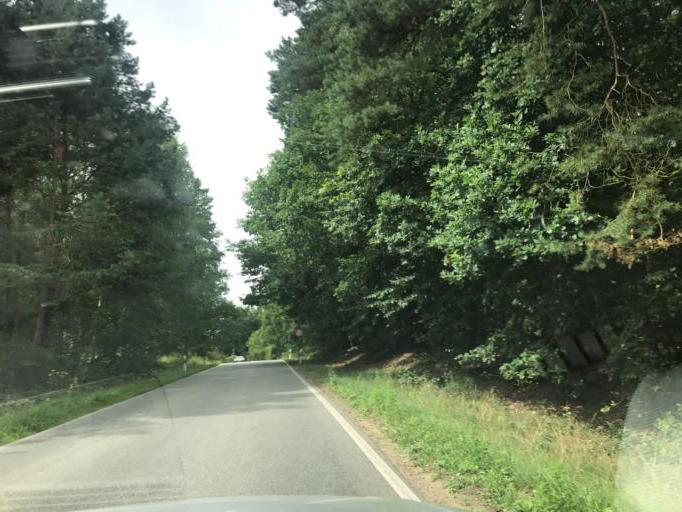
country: DE
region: Mecklenburg-Vorpommern
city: Rechlin
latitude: 53.2470
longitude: 12.6806
